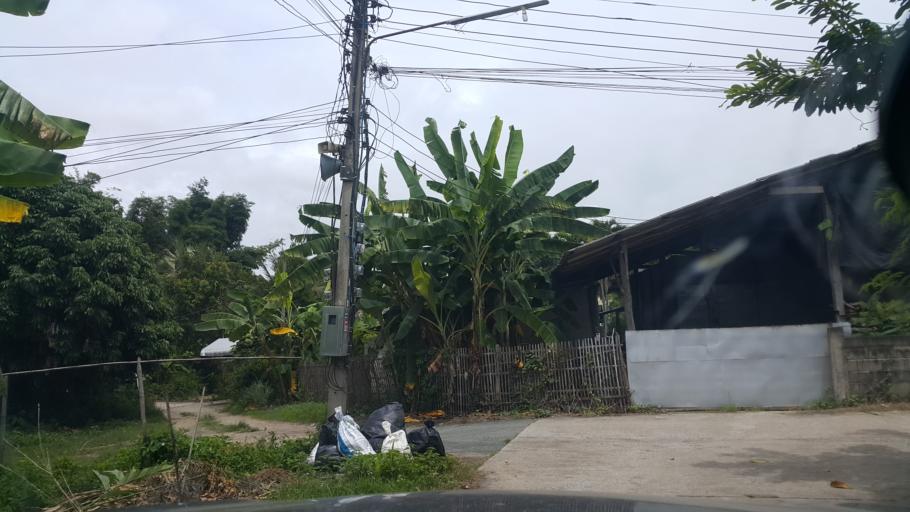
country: TH
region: Chiang Mai
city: Mae On
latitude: 18.7262
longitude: 99.2043
